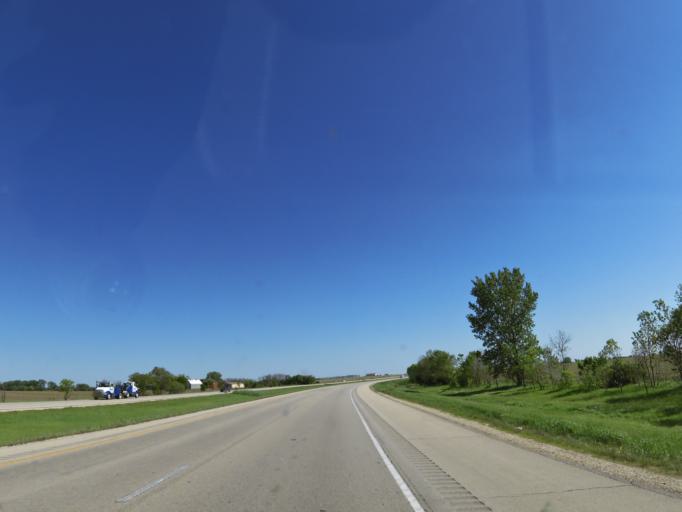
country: US
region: Illinois
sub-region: Ogle County
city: Rochelle
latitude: 41.8894
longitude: -89.0124
